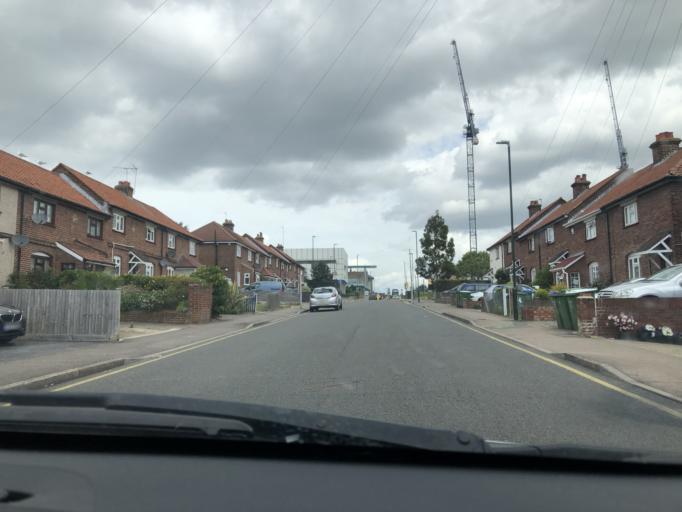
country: GB
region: England
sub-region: Greater London
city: Bexley
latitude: 51.4538
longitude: 0.1486
